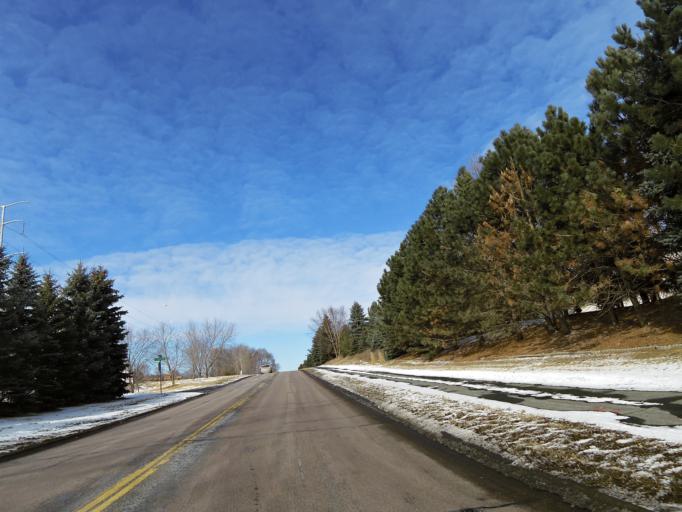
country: US
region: Minnesota
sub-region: Hennepin County
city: Eden Prairie
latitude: 44.8247
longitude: -93.4291
